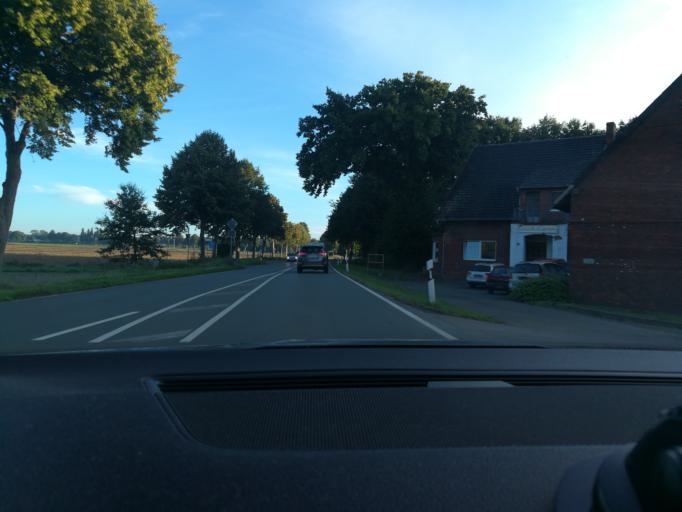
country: DE
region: North Rhine-Westphalia
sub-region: Regierungsbezirk Detmold
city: Minden
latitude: 52.3270
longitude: 8.8829
